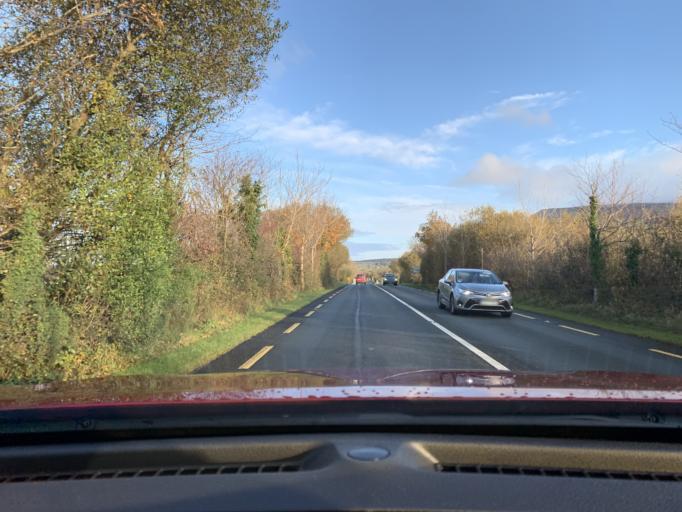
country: IE
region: Connaught
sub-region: Sligo
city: Sligo
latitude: 54.3322
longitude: -8.5019
